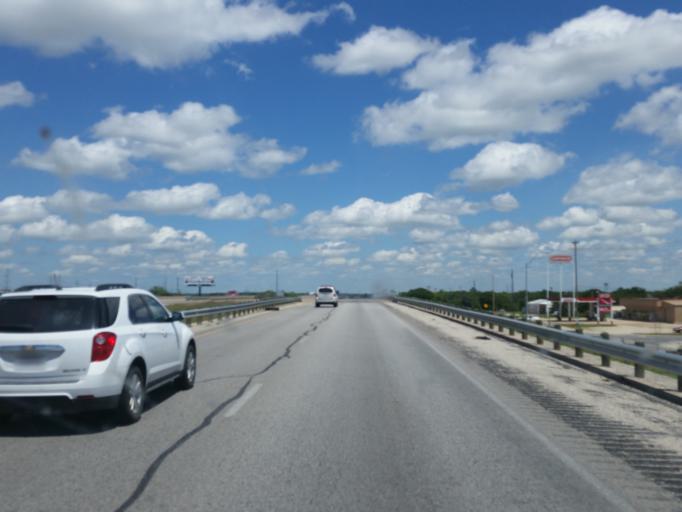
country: US
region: Texas
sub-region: Callahan County
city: Clyde
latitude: 32.4153
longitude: -99.5095
